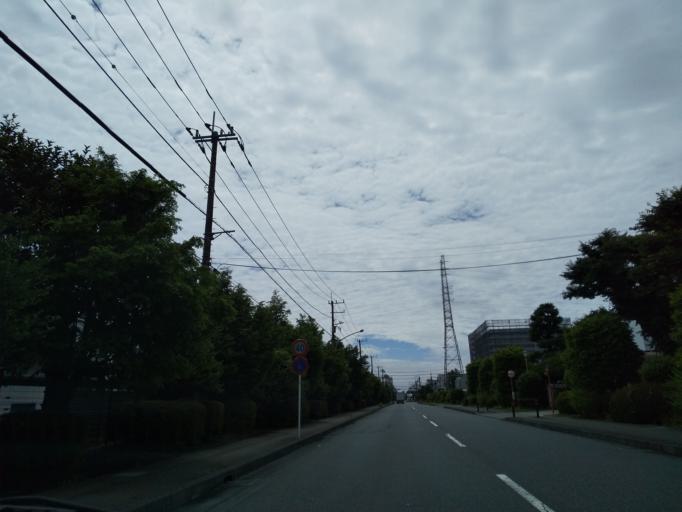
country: JP
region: Kanagawa
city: Zama
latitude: 35.5207
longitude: 139.3512
